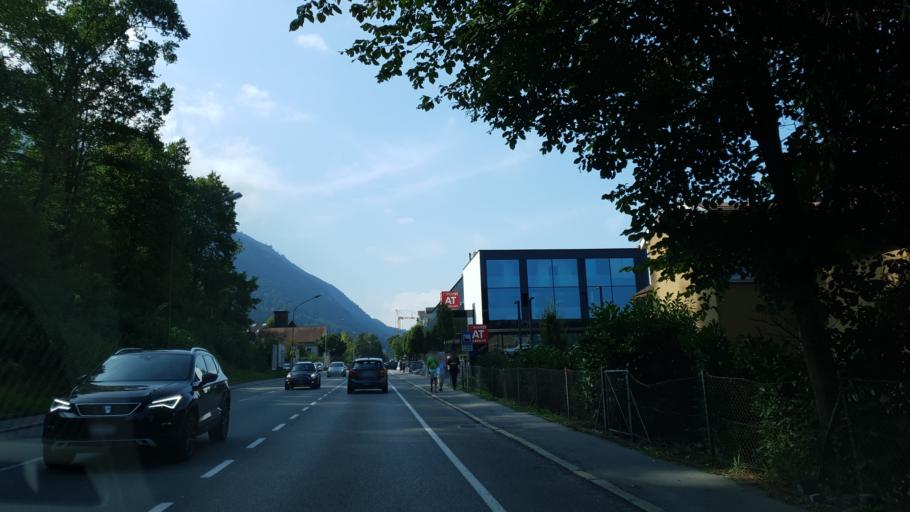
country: AT
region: Vorarlberg
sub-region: Politischer Bezirk Feldkirch
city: Feldkirch
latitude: 47.2277
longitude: 9.5842
